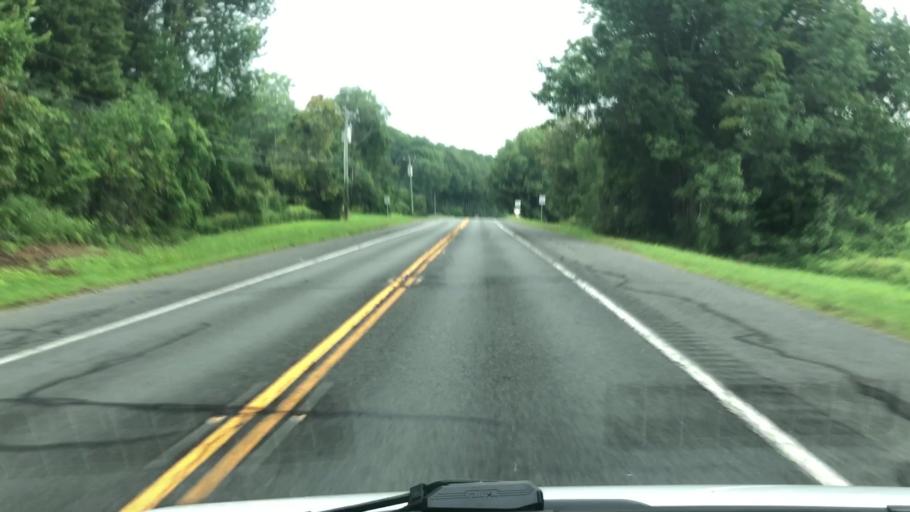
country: US
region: Massachusetts
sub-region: Berkshire County
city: Lanesborough
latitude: 42.5801
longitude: -73.2501
